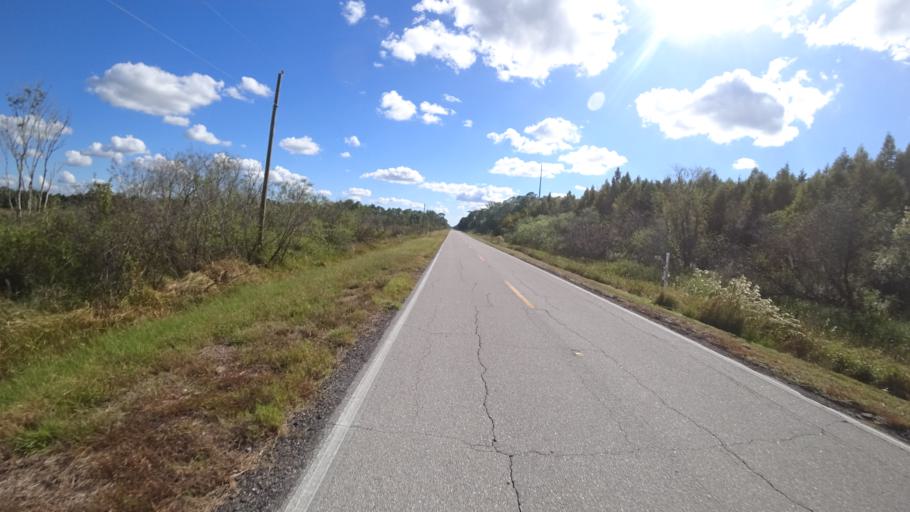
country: US
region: Florida
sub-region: Sarasota County
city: Warm Mineral Springs
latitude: 27.2542
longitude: -82.1218
